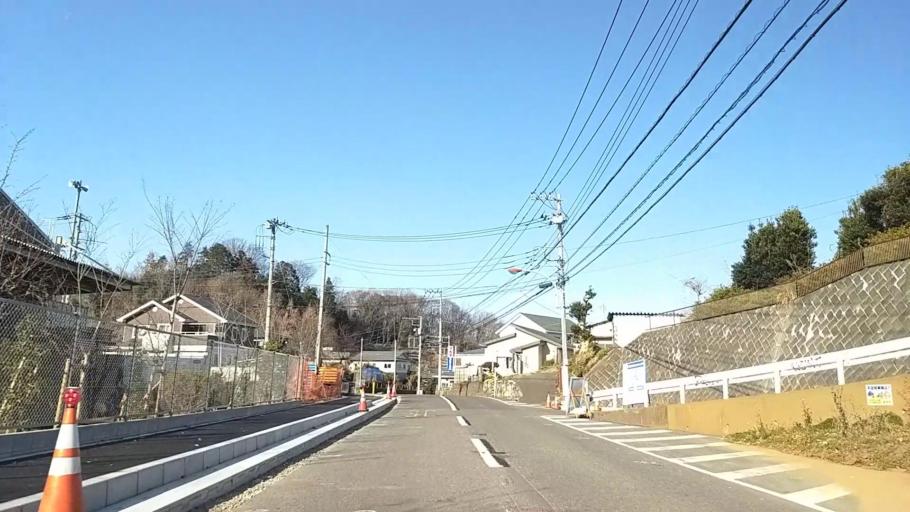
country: JP
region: Kanagawa
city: Atsugi
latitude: 35.4531
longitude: 139.3119
